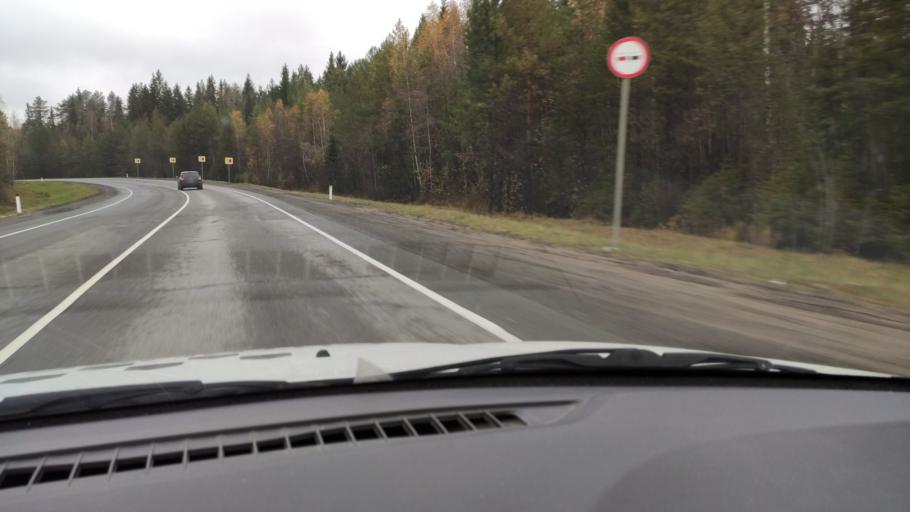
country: RU
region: Kirov
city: Belaya Kholunitsa
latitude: 58.9049
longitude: 50.9436
